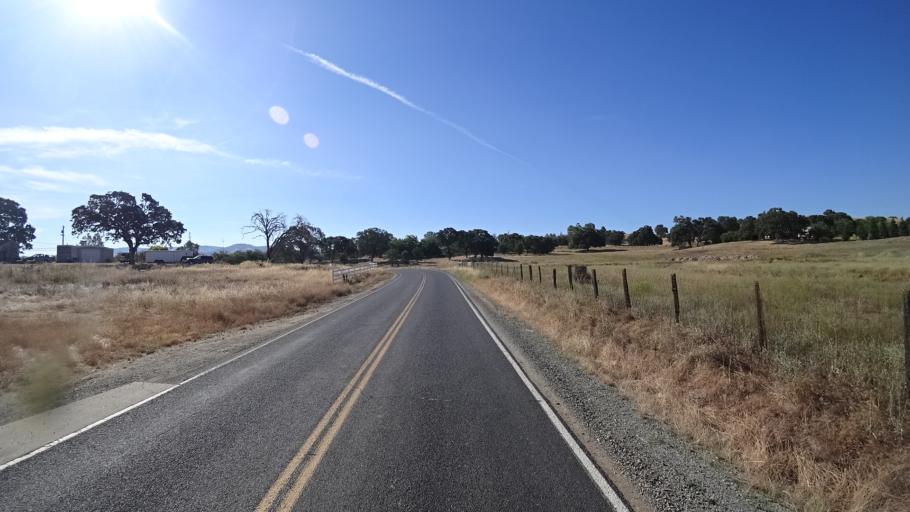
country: US
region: California
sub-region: Calaveras County
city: Valley Springs
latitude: 38.1845
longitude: -120.8193
